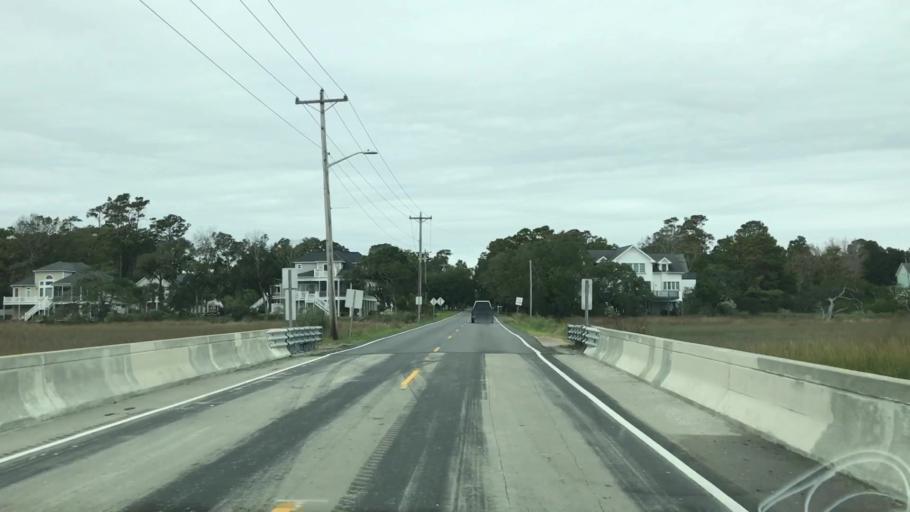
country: US
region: South Carolina
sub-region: Horry County
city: Garden City
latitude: 33.5835
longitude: -78.9981
